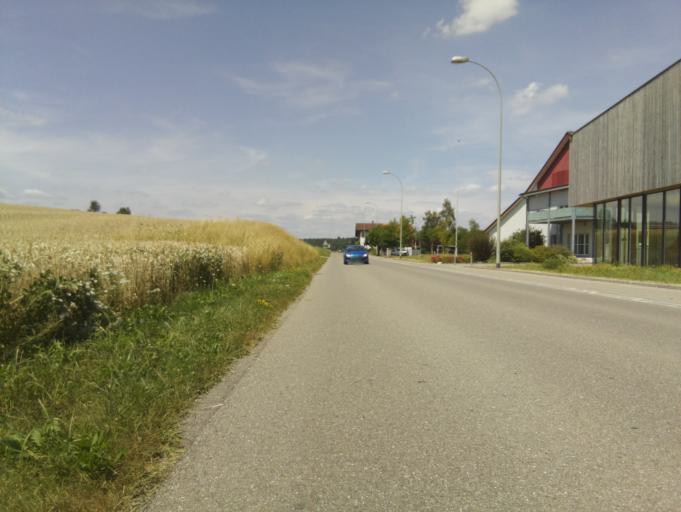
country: CH
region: Zurich
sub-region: Bezirk Andelfingen
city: Marthalen
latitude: 47.6306
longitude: 8.6492
